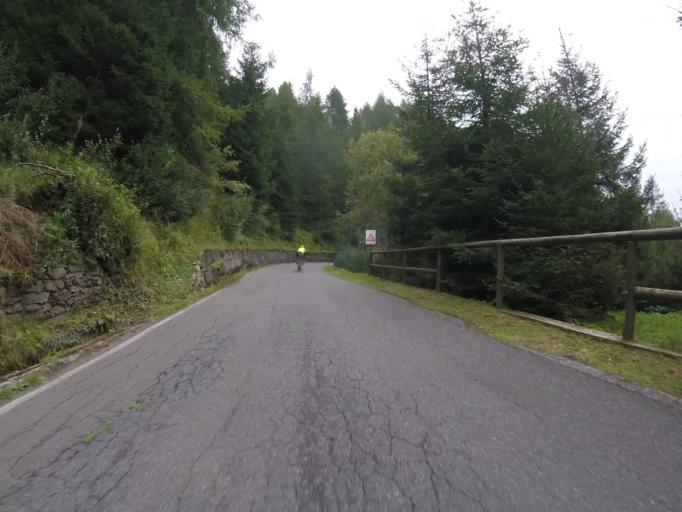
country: IT
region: Lombardy
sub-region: Provincia di Brescia
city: Monno
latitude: 46.2393
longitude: 10.3202
